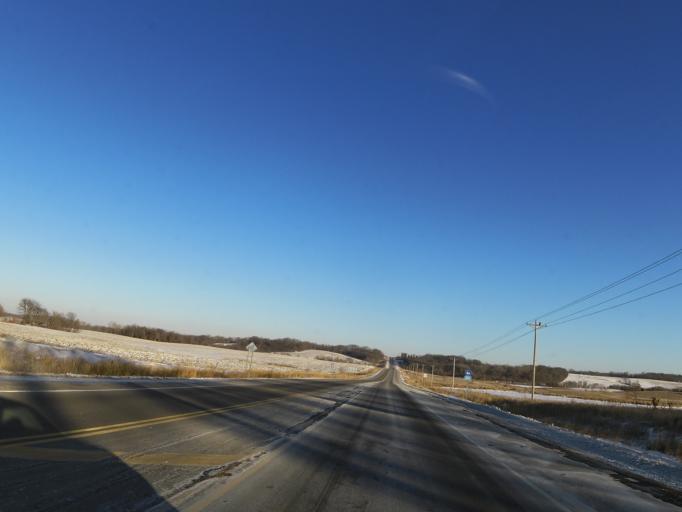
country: US
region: Minnesota
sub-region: Rice County
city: Lonsdale
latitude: 44.5438
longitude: -93.4408
